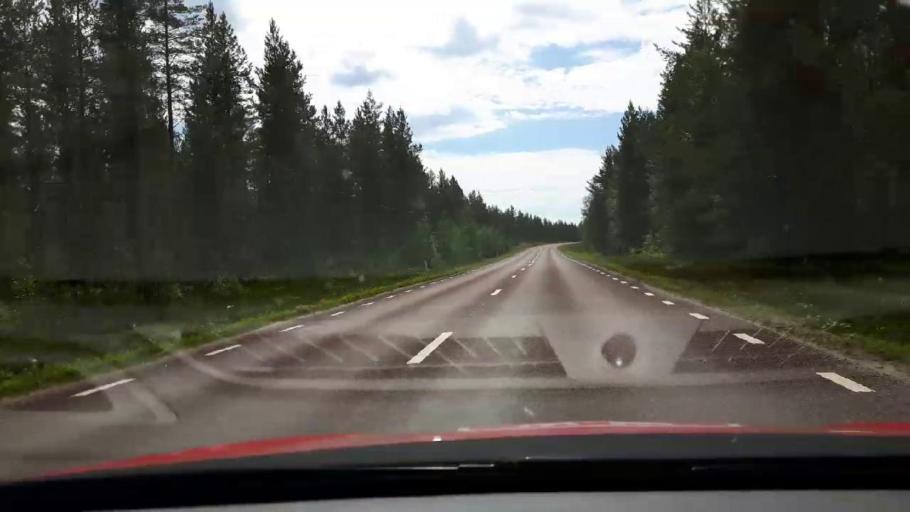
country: SE
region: Jaemtland
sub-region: Harjedalens Kommun
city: Sveg
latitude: 62.1087
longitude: 14.9709
